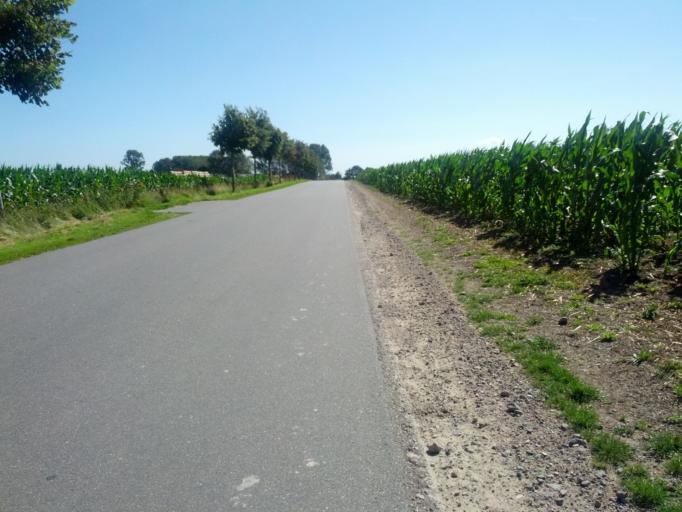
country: DE
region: Mecklenburg-Vorpommern
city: Bastorf
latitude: 54.1282
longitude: 11.6842
